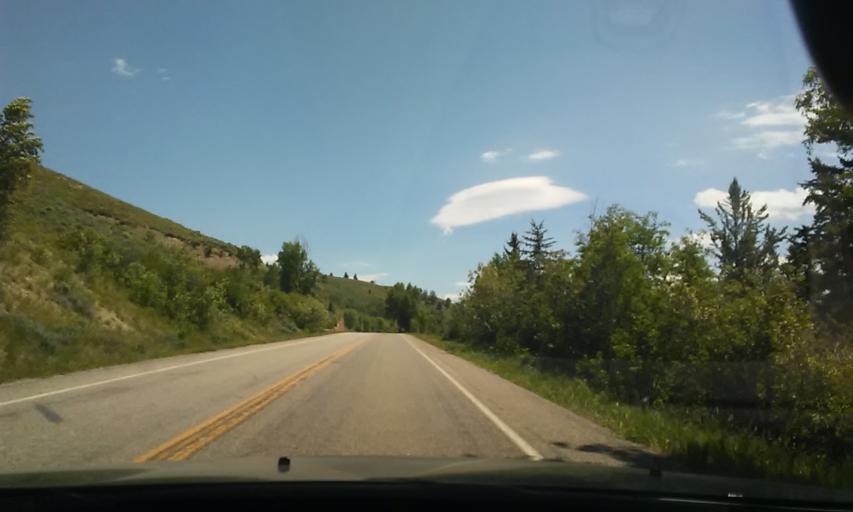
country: US
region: Wyoming
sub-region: Teton County
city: Jackson
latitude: 43.8381
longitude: -110.4951
